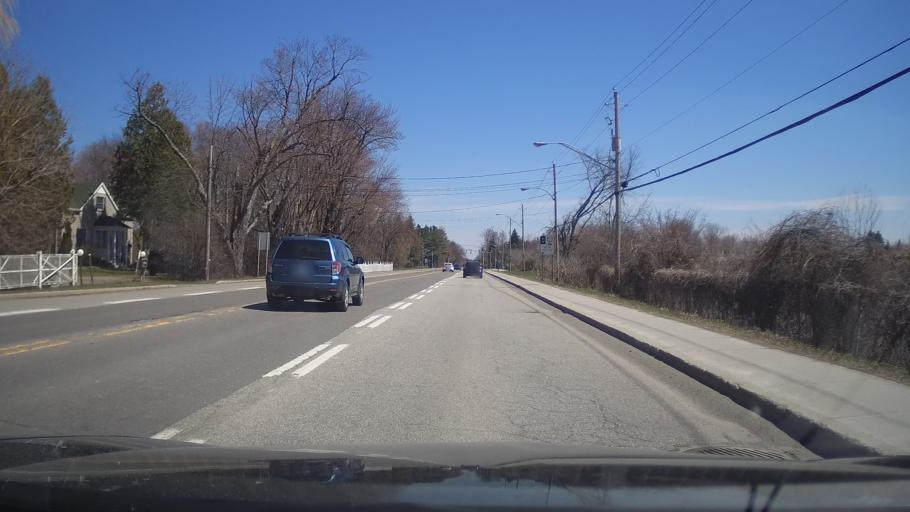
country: CA
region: Ontario
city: Bells Corners
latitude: 45.4035
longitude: -75.7972
